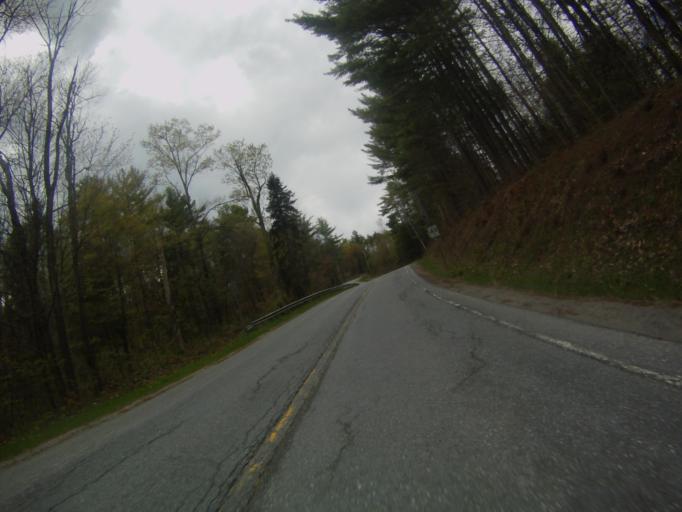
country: US
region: New York
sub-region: Essex County
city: Mineville
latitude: 44.0902
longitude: -73.5471
